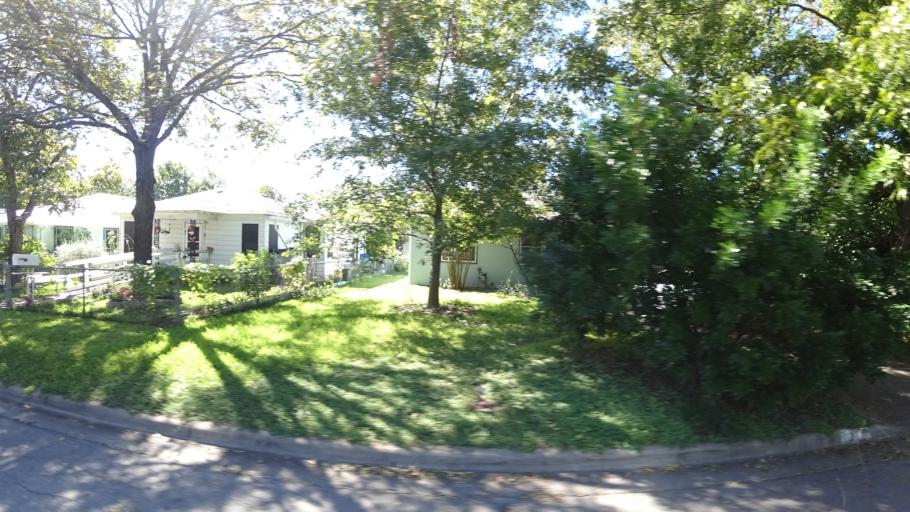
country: US
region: Texas
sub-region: Travis County
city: Austin
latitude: 30.3201
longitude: -97.7248
